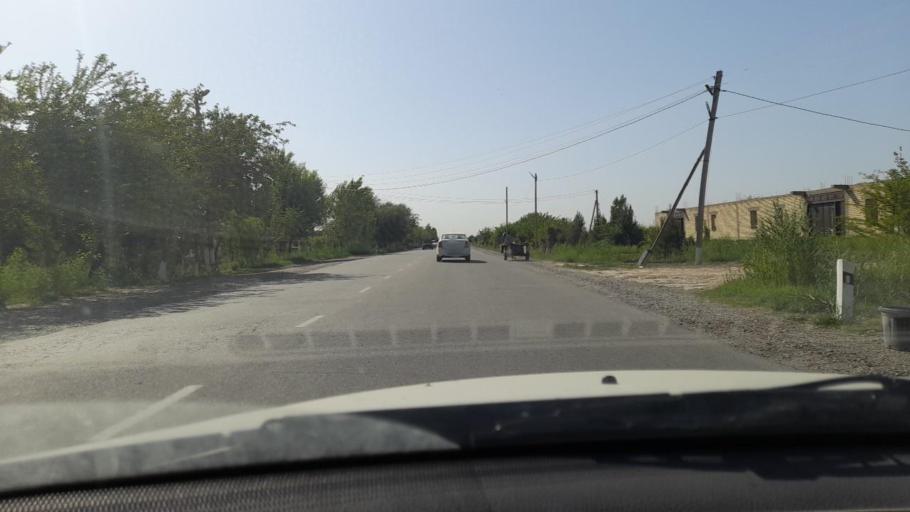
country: UZ
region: Bukhara
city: Romiton
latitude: 39.8977
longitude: 64.4097
